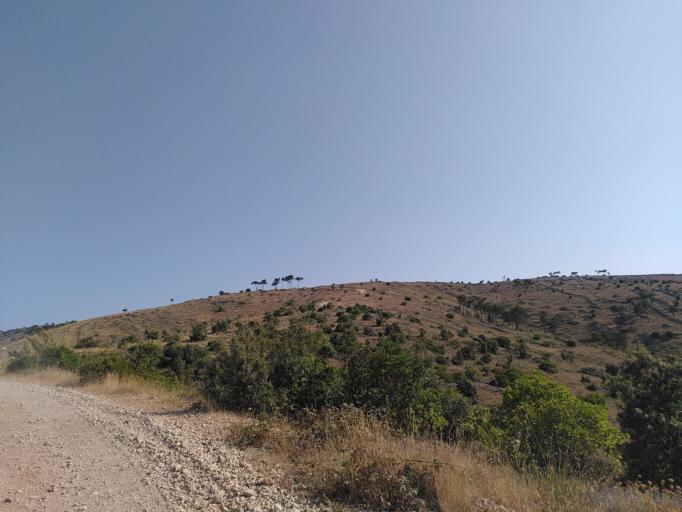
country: HR
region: Splitsko-Dalmatinska
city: Stari Grad
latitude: 43.1528
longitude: 16.5876
